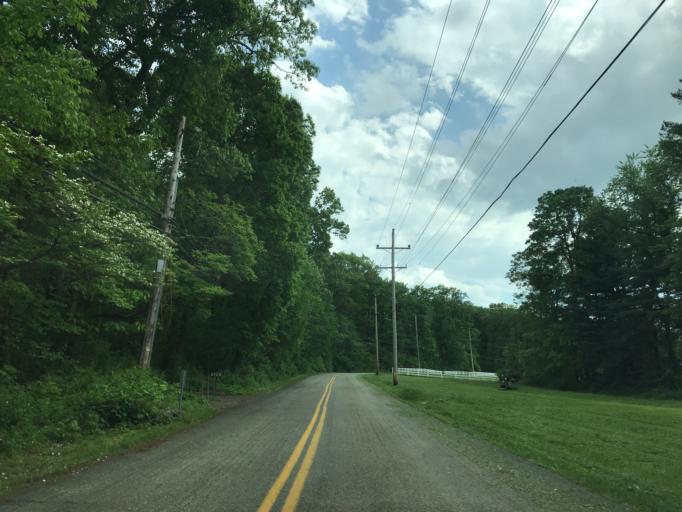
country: US
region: Pennsylvania
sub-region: York County
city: Susquehanna Trails
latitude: 39.6973
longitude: -76.3631
